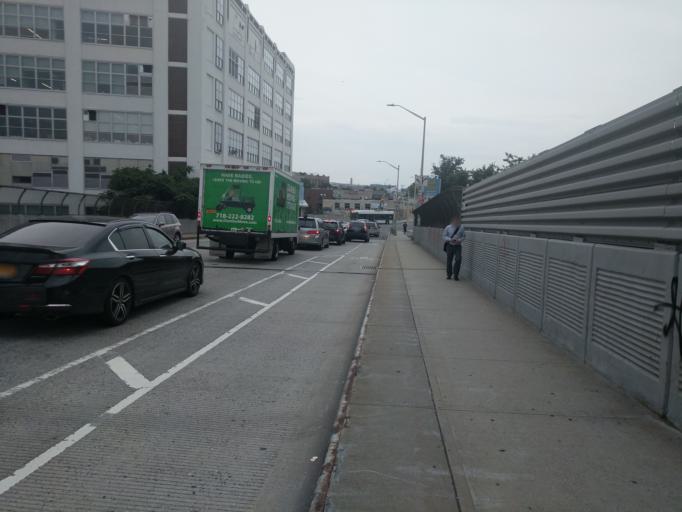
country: US
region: New York
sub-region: Queens County
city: Long Island City
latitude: 40.7514
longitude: -73.9246
